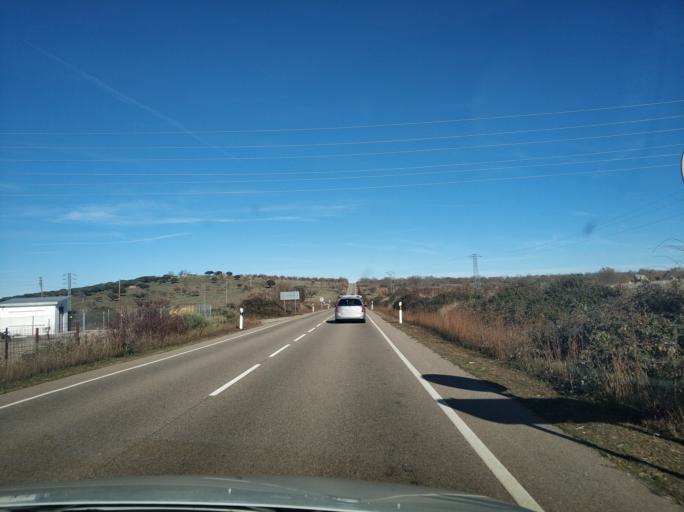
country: ES
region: Castille and Leon
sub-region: Provincia de Salamanca
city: Narros de Matalayegua
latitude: 40.6665
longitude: -5.8969
